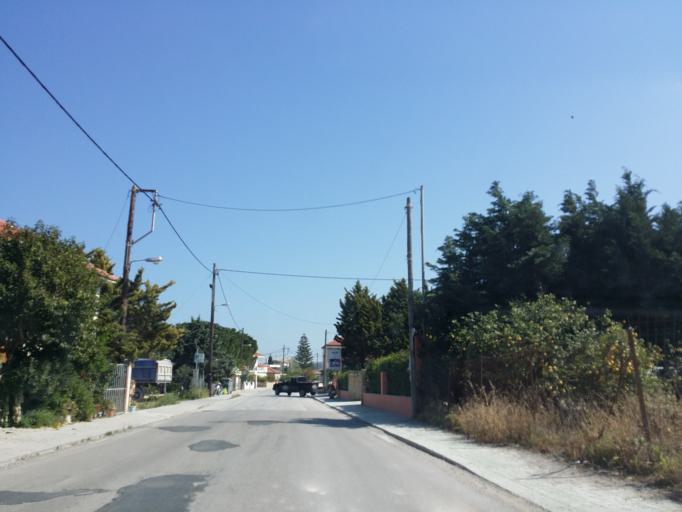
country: GR
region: Peloponnese
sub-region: Nomos Korinthias
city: Xylokastro
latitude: 38.0989
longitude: 22.5730
